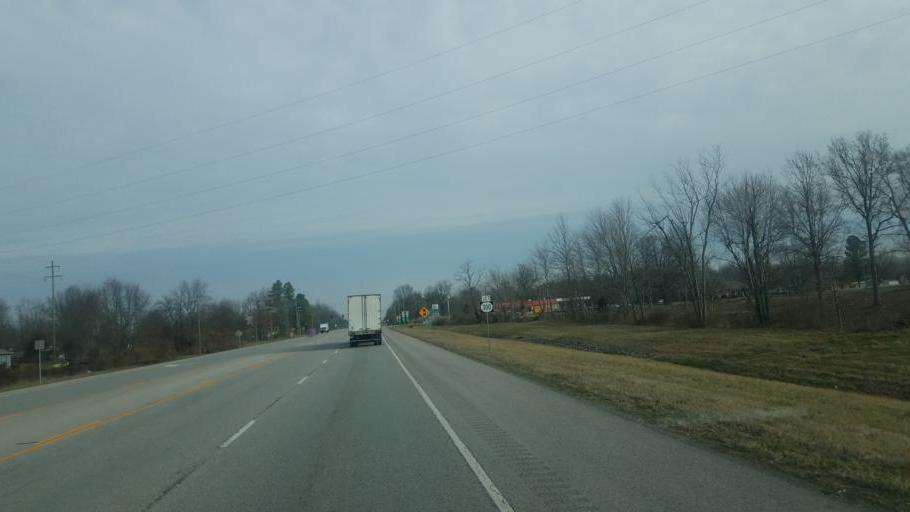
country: US
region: Kentucky
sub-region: Boyle County
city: Junction City
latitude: 37.5806
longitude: -84.7883
